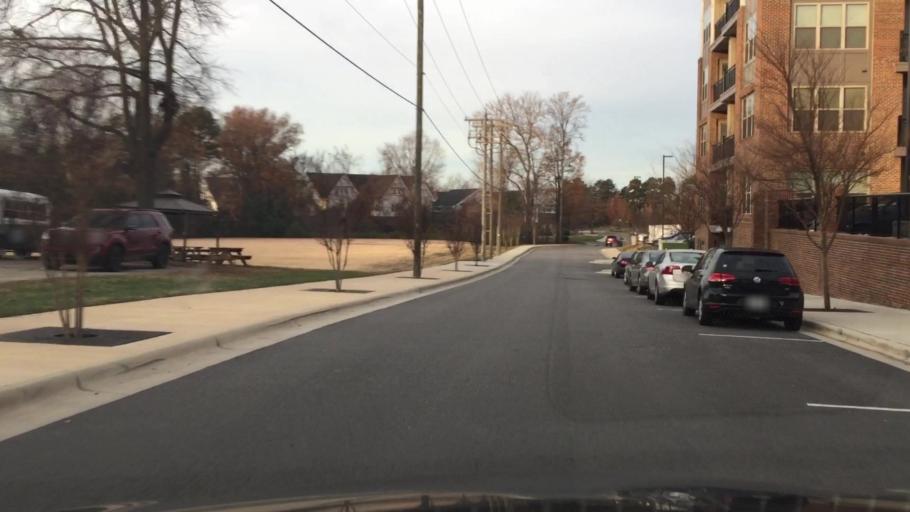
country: US
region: North Carolina
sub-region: Mecklenburg County
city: Cornelius
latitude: 35.5005
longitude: -80.8617
